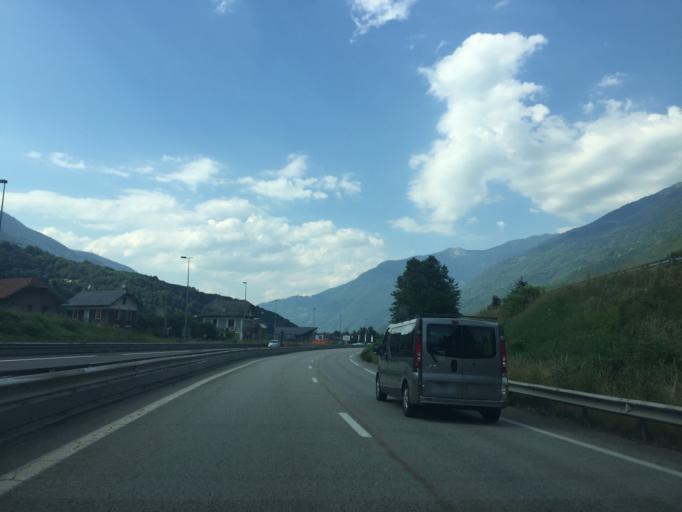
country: FR
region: Rhone-Alpes
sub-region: Departement de la Savoie
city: La Bathie
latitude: 45.5941
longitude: 6.4476
